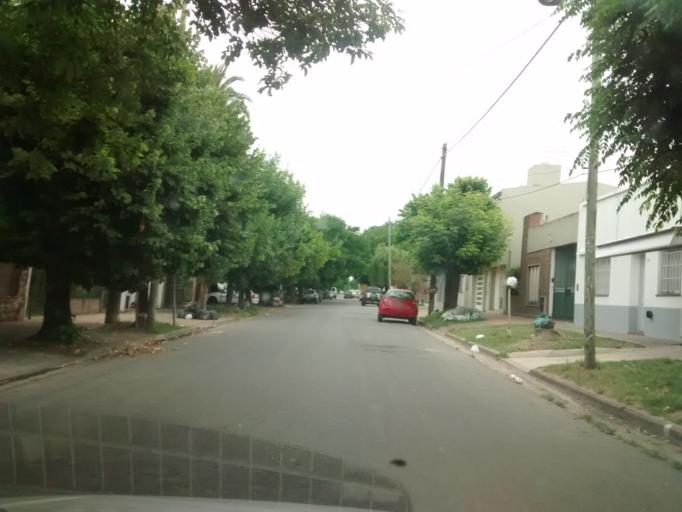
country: AR
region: Buenos Aires
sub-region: Partido de La Plata
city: La Plata
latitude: -34.9206
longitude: -57.9123
